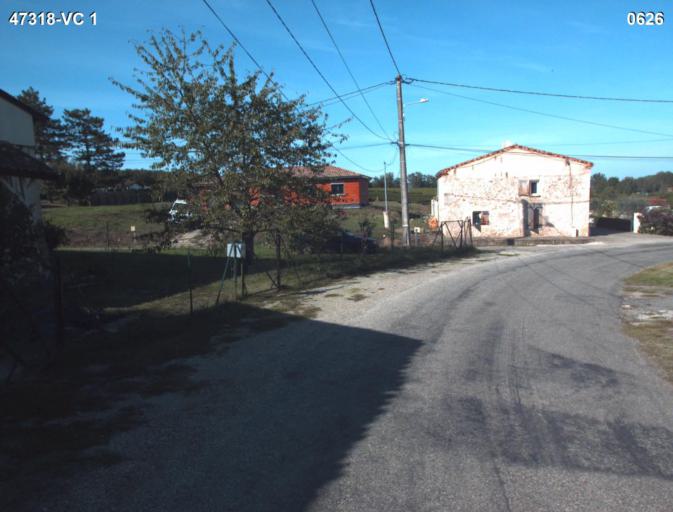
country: FR
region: Aquitaine
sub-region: Departement du Lot-et-Garonne
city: Vianne
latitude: 44.2238
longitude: 0.3203
